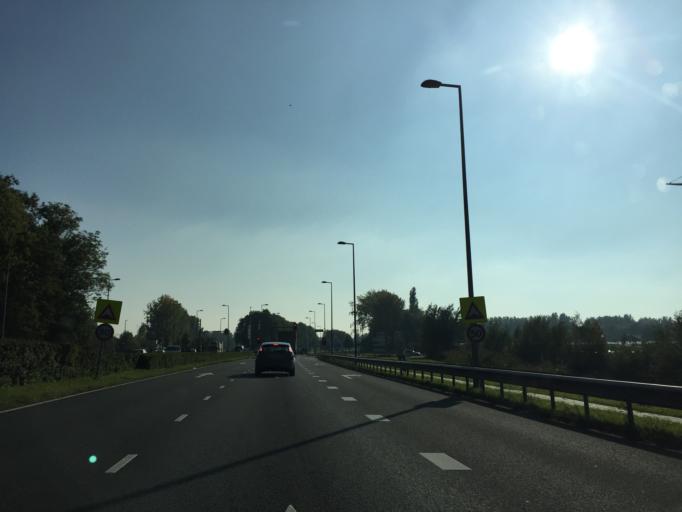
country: NL
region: South Holland
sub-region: Gemeente Rotterdam
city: Rotterdam
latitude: 51.9572
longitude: 4.4615
